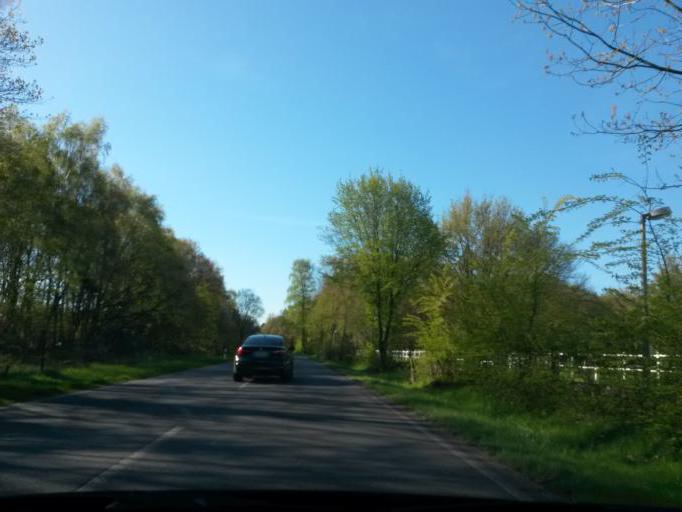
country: DE
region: Schleswig-Holstein
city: Pinneberg
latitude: 53.6283
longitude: 9.7773
